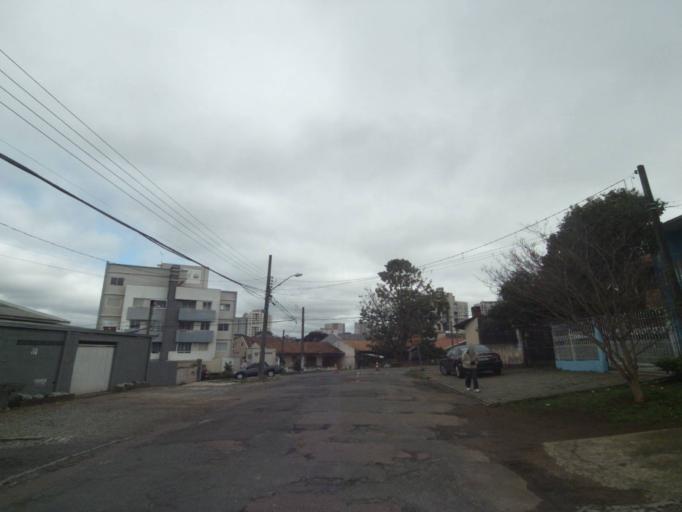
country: BR
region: Parana
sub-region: Curitiba
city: Curitiba
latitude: -25.4999
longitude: -49.2905
